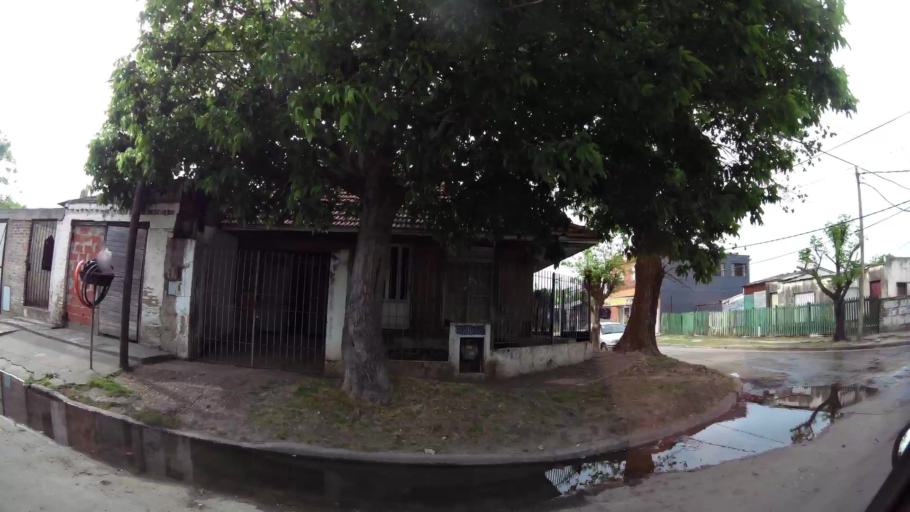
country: AR
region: Buenos Aires
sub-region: Partido de Quilmes
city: Quilmes
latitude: -34.7171
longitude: -58.2441
